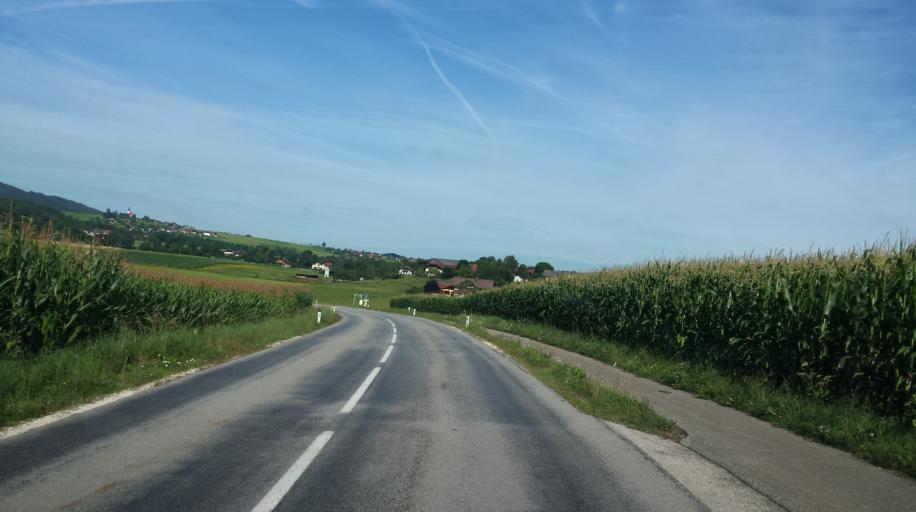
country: AT
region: Upper Austria
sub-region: Politischer Bezirk Vocklabruck
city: Sankt Georgen im Attergau
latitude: 47.9474
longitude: 13.4557
